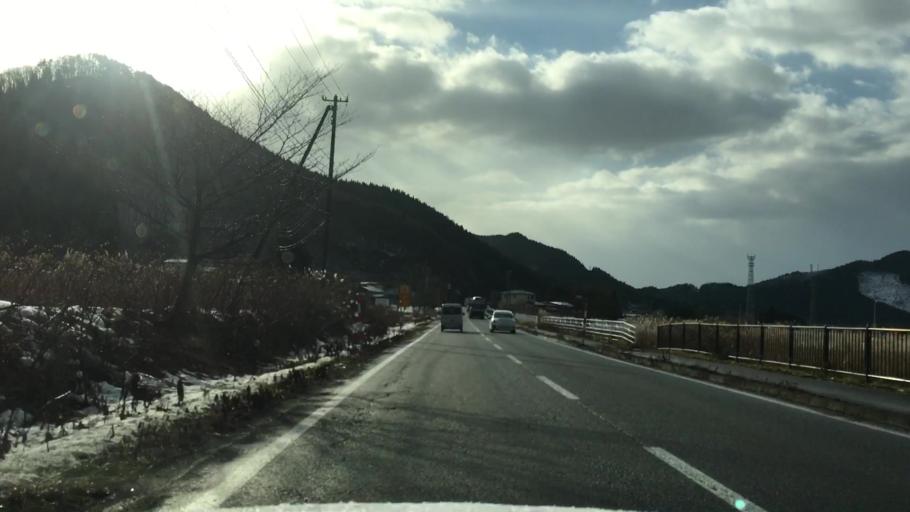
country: JP
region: Akita
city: Odate
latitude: 40.3546
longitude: 140.5995
